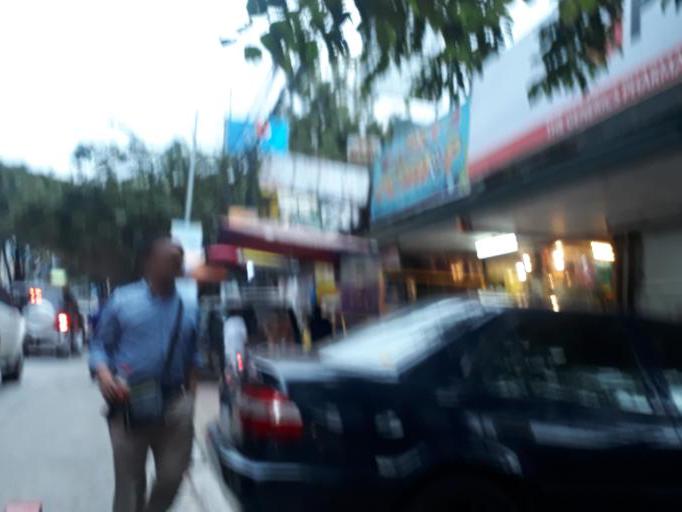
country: PH
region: Metro Manila
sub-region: Quezon City
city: Quezon City
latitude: 14.6785
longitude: 121.0822
